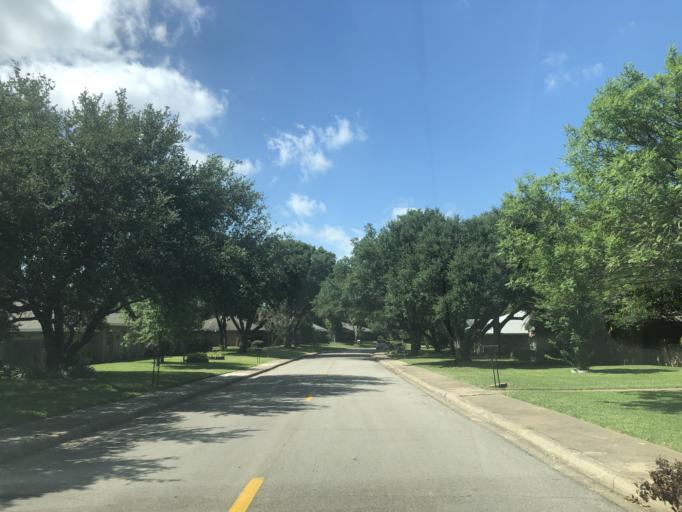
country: US
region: Texas
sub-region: Dallas County
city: Duncanville
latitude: 32.6549
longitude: -96.9274
